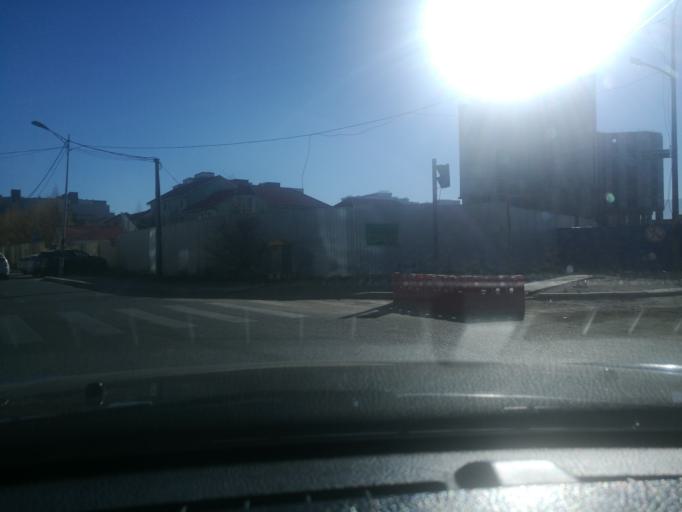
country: MN
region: Ulaanbaatar
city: Ulaanbaatar
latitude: 47.9121
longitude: 106.9234
